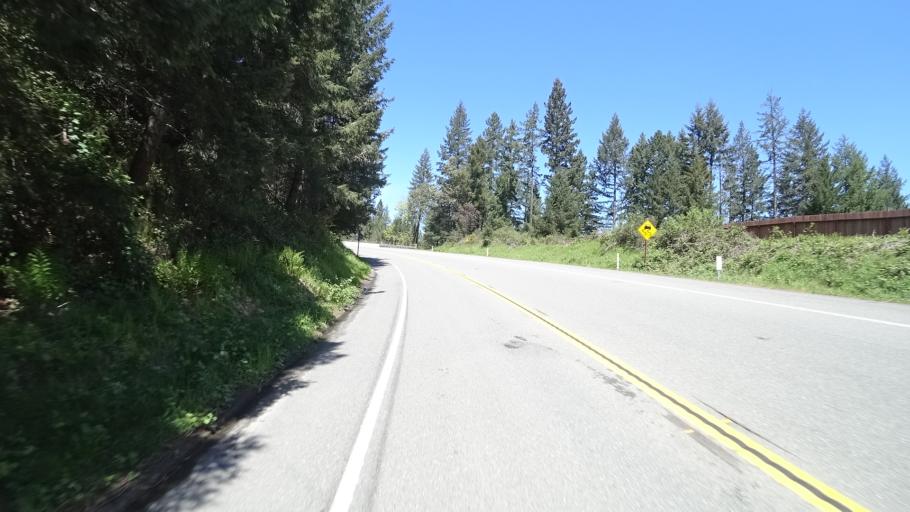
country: US
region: California
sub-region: Humboldt County
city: Blue Lake
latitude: 40.9149
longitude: -123.8255
